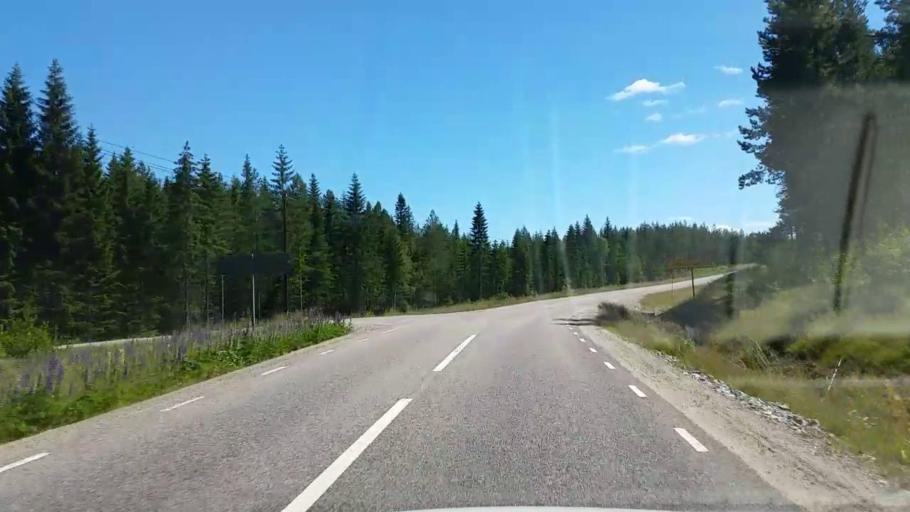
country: SE
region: Gaevleborg
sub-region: Ovanakers Kommun
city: Edsbyn
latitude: 61.5750
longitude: 15.6652
